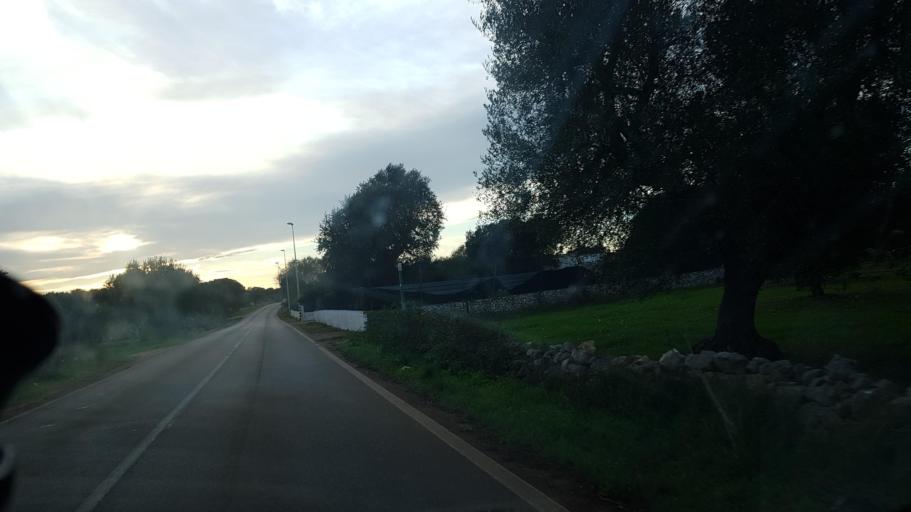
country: IT
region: Apulia
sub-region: Provincia di Brindisi
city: San Michele Salentino
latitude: 40.6460
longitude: 17.6616
